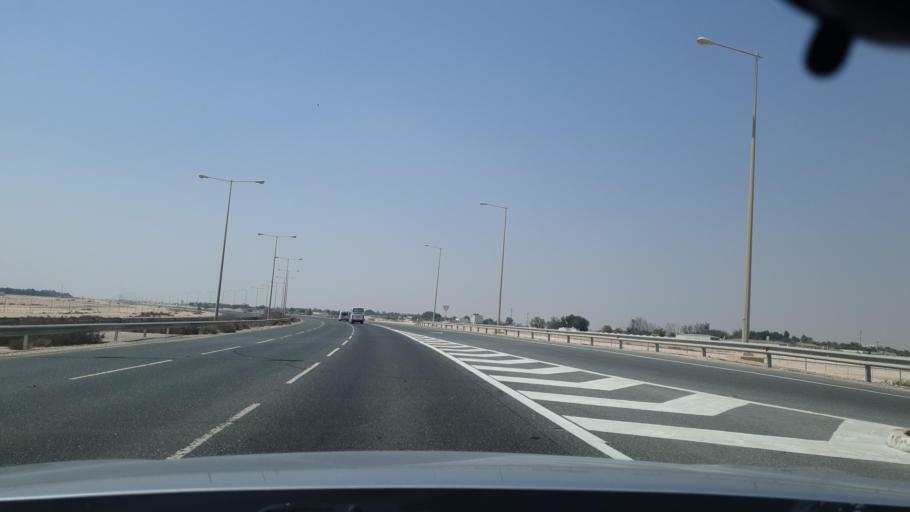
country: QA
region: Al Khawr
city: Al Khawr
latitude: 25.7576
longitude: 51.4685
